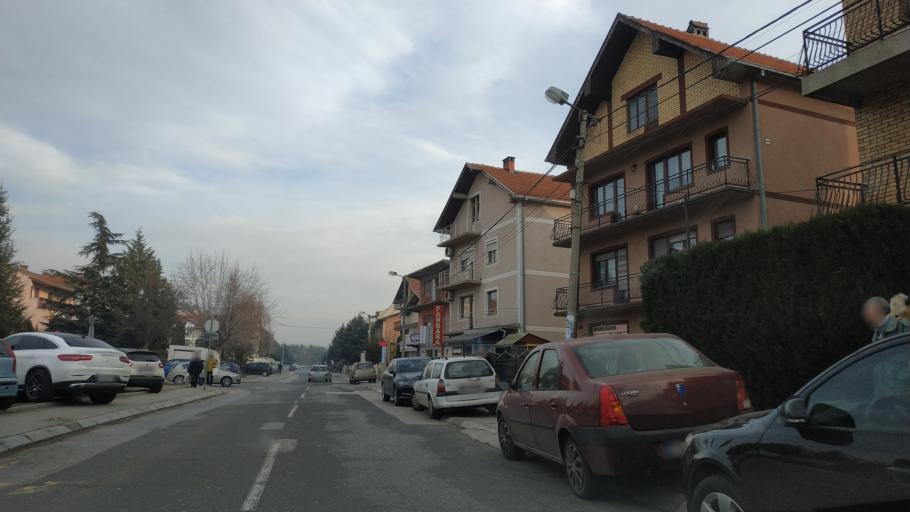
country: RS
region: Central Serbia
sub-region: Nisavski Okrug
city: Nis
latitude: 43.3192
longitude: 21.9321
